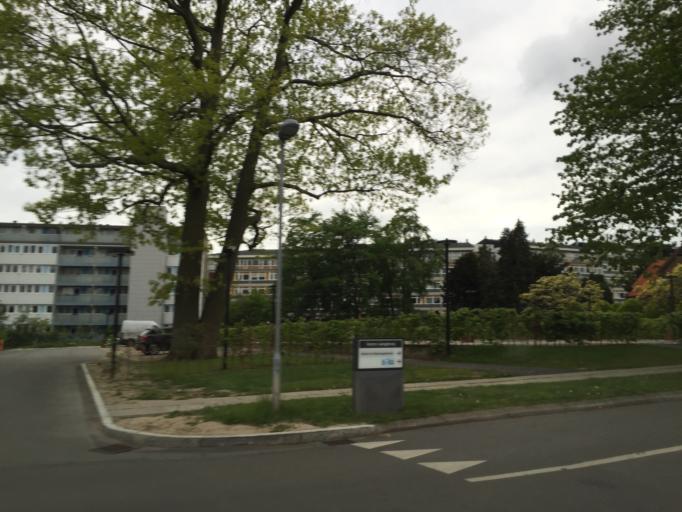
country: DK
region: Capital Region
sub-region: Frederiksberg Kommune
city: Frederiksberg
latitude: 55.7118
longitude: 12.5403
